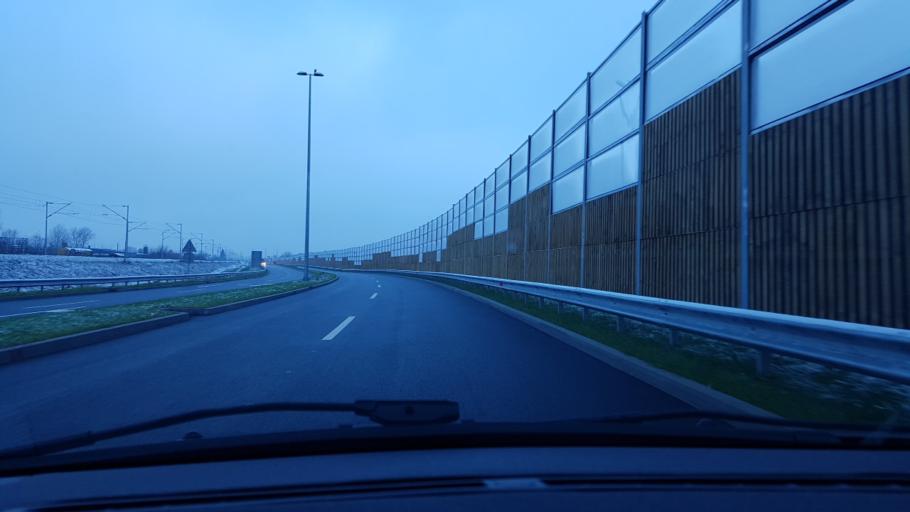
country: HR
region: Zagrebacka
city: Zapresic
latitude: 45.8518
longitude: 15.8056
